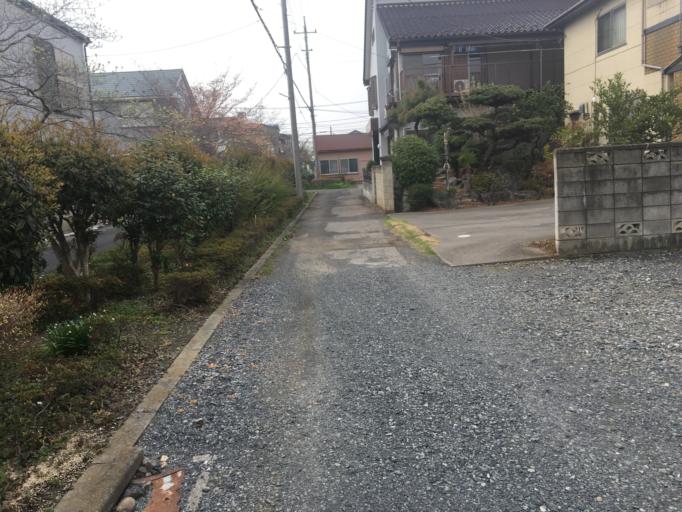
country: JP
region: Saitama
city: Sugito
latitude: 36.0279
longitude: 139.7294
